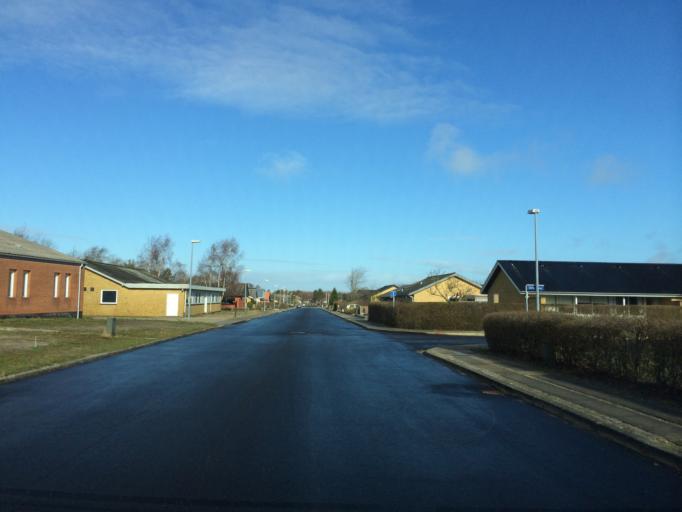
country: DK
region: Central Jutland
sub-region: Holstebro Kommune
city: Ulfborg
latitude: 56.2724
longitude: 8.3150
